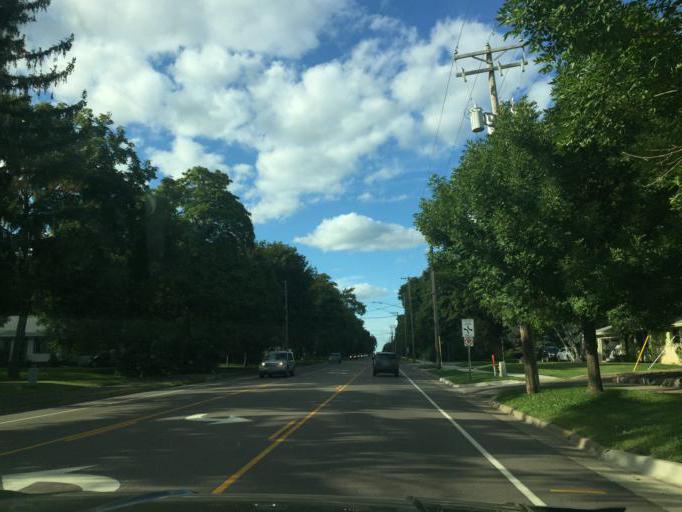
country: US
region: Minnesota
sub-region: Ramsey County
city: Roseville
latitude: 44.9998
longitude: -93.1463
